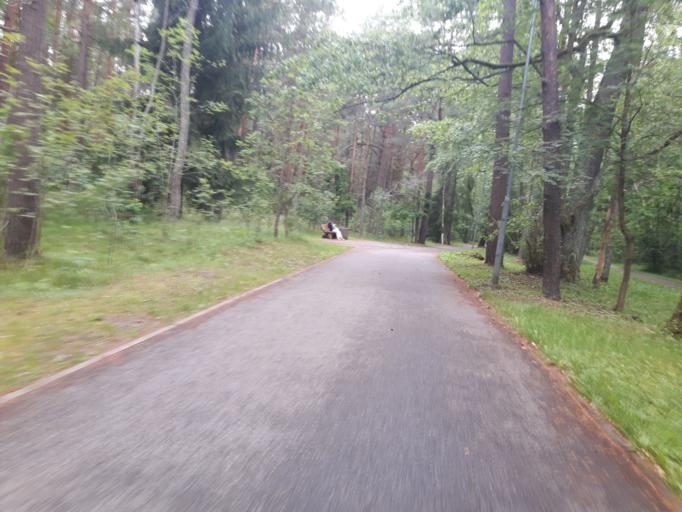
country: LT
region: Klaipedos apskritis
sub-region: Klaipeda
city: Klaipeda
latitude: 55.7397
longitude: 21.1248
